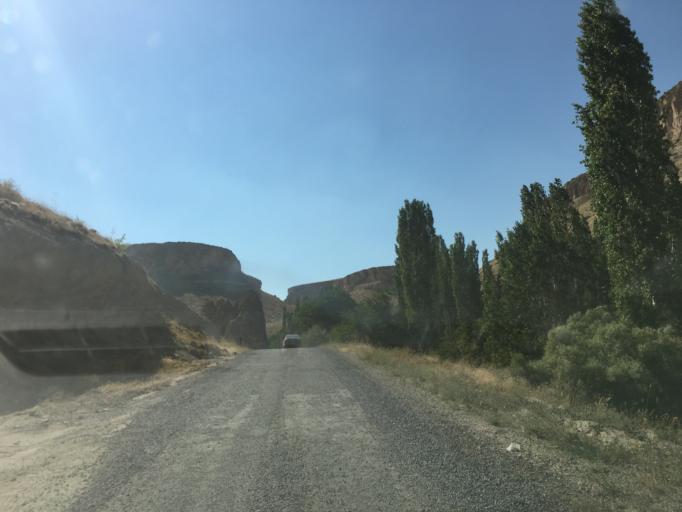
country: TR
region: Kayseri
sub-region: Yesilhisar
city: Yesilhisar
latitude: 38.3447
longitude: 34.9679
